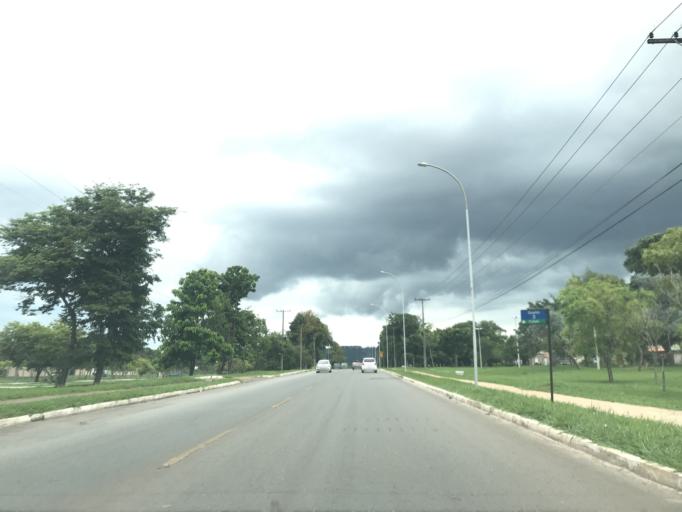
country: BR
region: Federal District
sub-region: Brasilia
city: Brasilia
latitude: -15.6537
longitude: -47.8140
